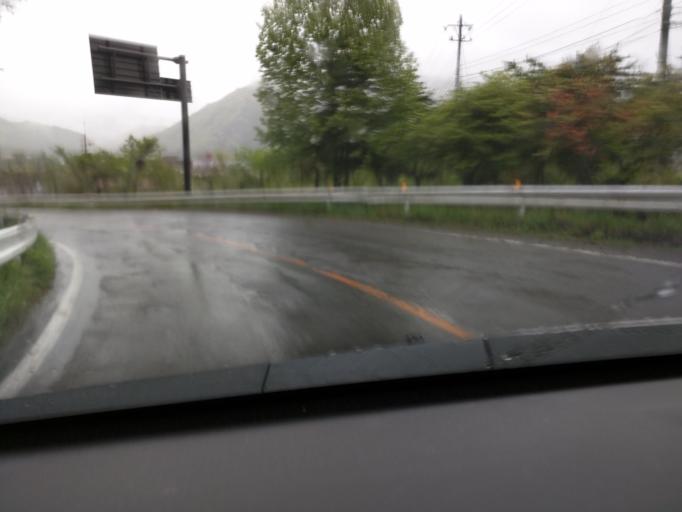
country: JP
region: Fukushima
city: Inawashiro
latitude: 37.6055
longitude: 140.1259
